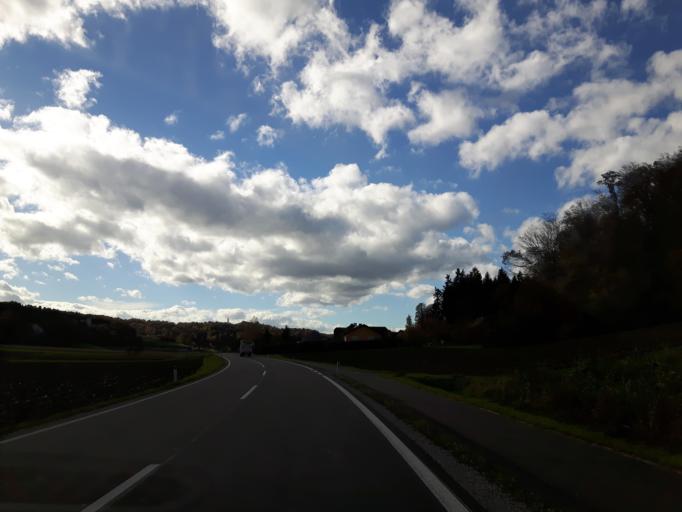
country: AT
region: Styria
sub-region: Politischer Bezirk Suedoststeiermark
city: Paldau
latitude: 46.9473
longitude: 15.8117
